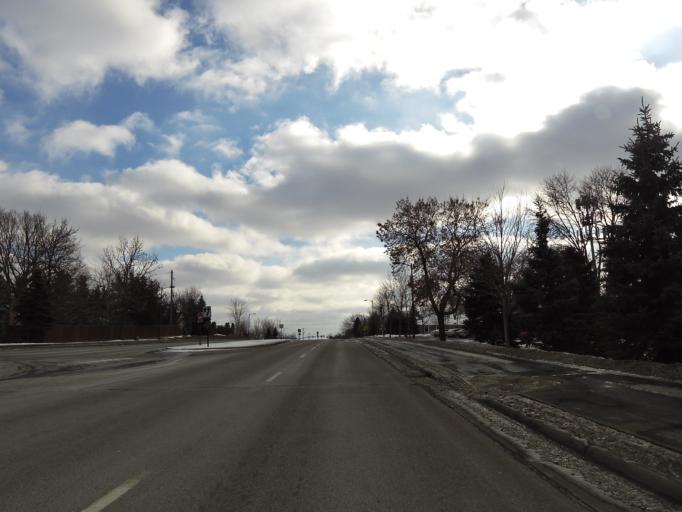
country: US
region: Minnesota
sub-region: Hennepin County
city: Eden Prairie
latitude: 44.8417
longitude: -93.4807
